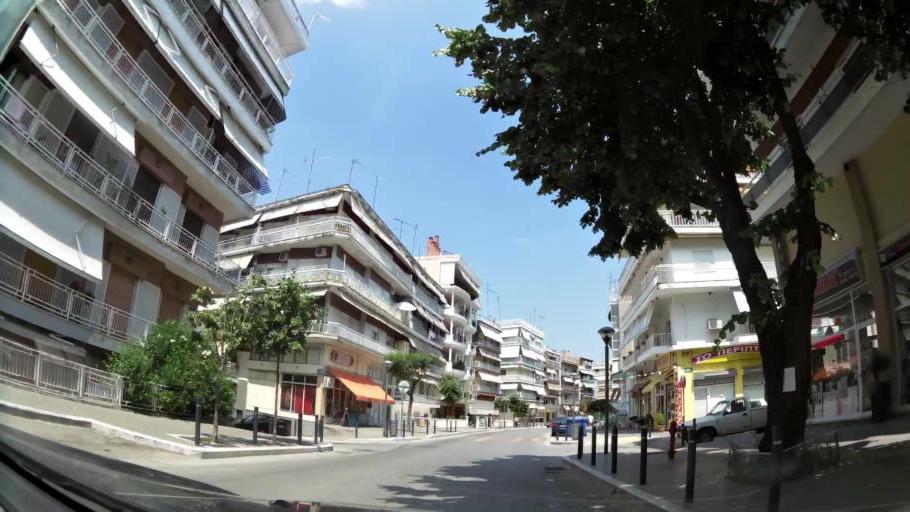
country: GR
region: Central Macedonia
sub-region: Nomos Imathias
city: Veroia
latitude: 40.5289
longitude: 22.2028
